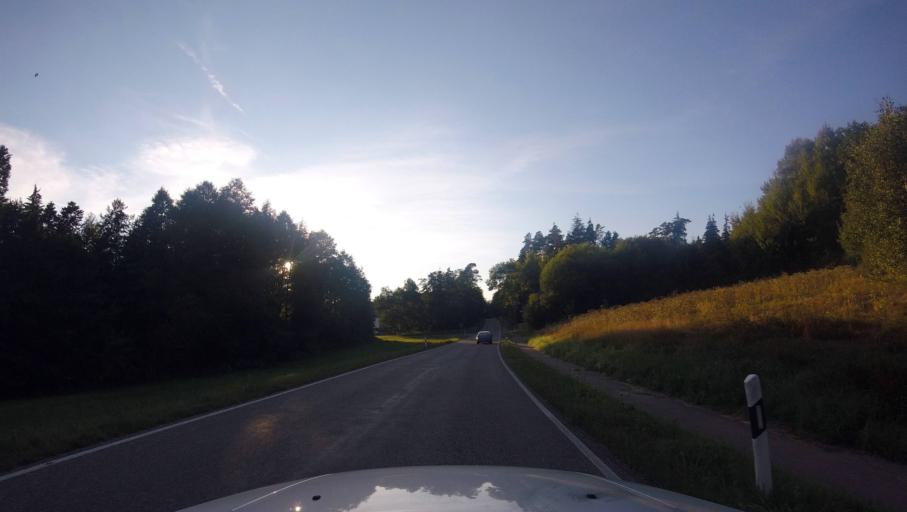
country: DE
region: Baden-Wuerttemberg
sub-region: Regierungsbezirk Stuttgart
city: Kaisersbach
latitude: 48.9124
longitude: 9.6751
